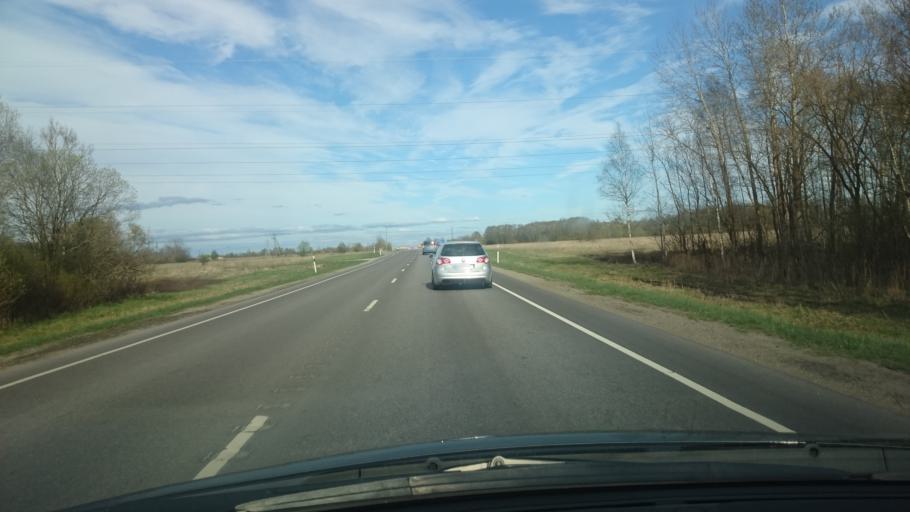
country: EE
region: Ida-Virumaa
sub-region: Sillamaee linn
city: Sillamae
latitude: 59.3913
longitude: 27.7176
